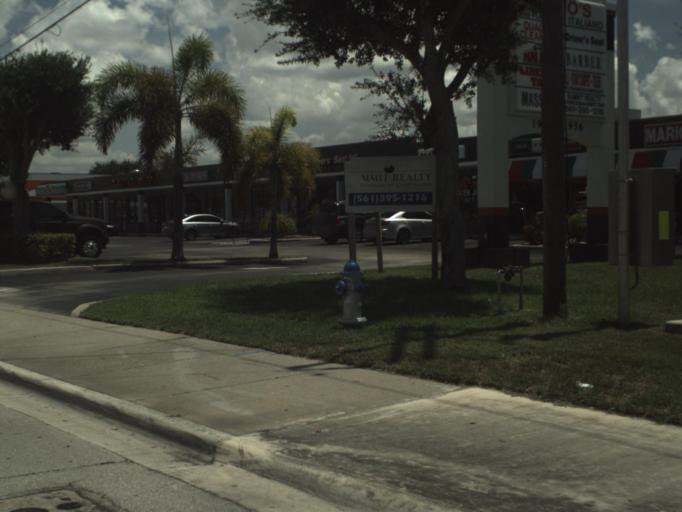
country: US
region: Florida
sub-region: Martin County
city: Stuart
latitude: 27.1816
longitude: -80.2406
